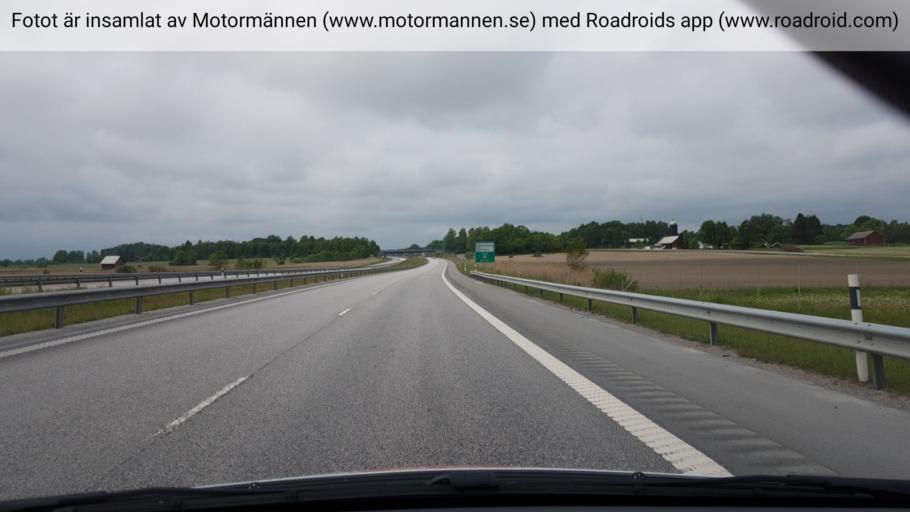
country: SE
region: OErebro
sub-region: Lindesbergs Kommun
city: Fellingsbro
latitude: 59.3311
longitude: 15.5194
